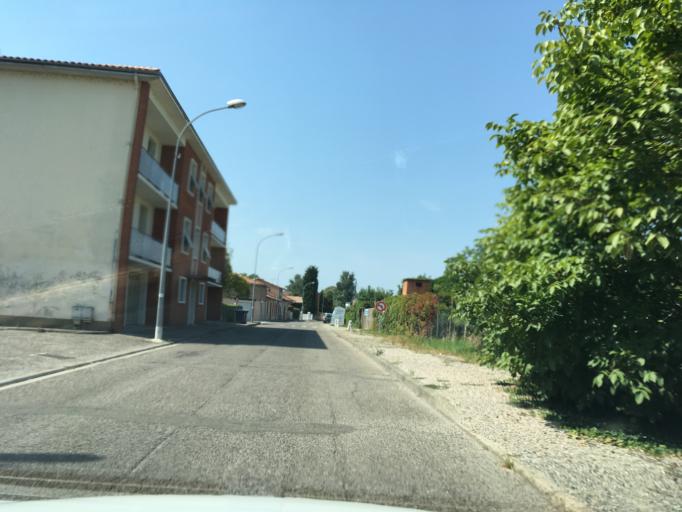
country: FR
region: Midi-Pyrenees
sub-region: Departement du Tarn-et-Garonne
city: Montauban
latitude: 44.0188
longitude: 1.3471
